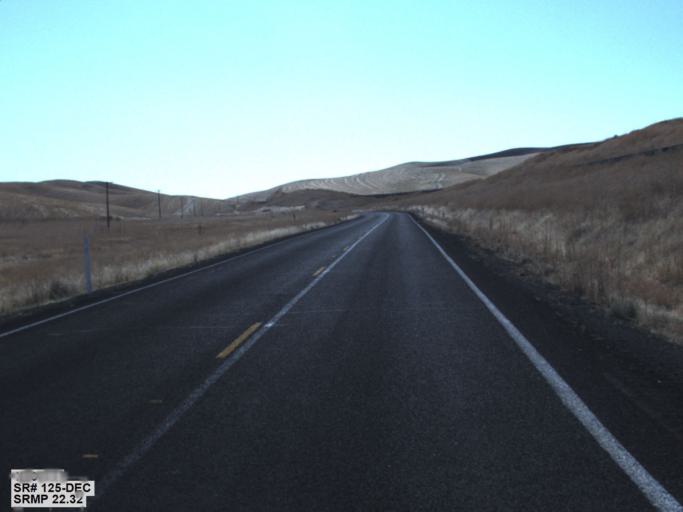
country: US
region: Washington
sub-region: Walla Walla County
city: Waitsburg
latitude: 46.2800
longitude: -118.3444
